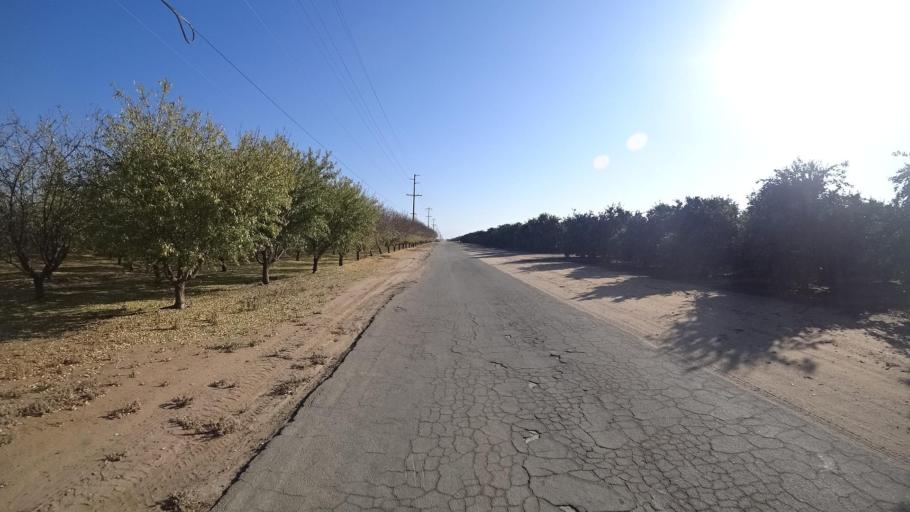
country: US
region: California
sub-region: Tulare County
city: Richgrove
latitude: 35.7327
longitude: -119.1277
